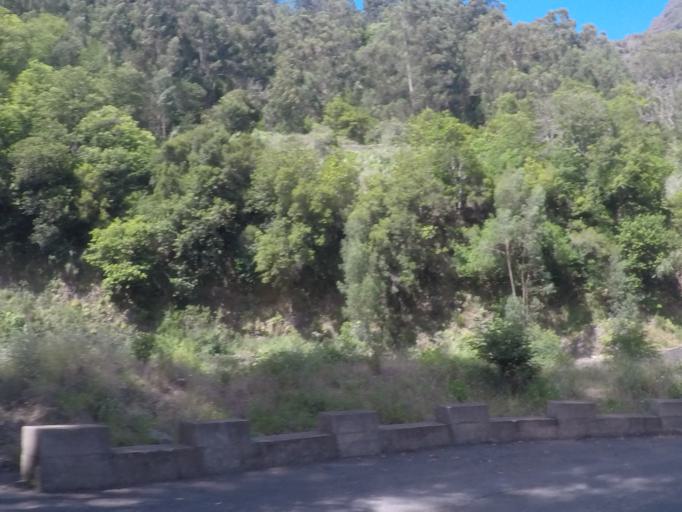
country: PT
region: Madeira
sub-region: Camara de Lobos
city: Curral das Freiras
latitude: 32.7156
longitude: -16.9775
